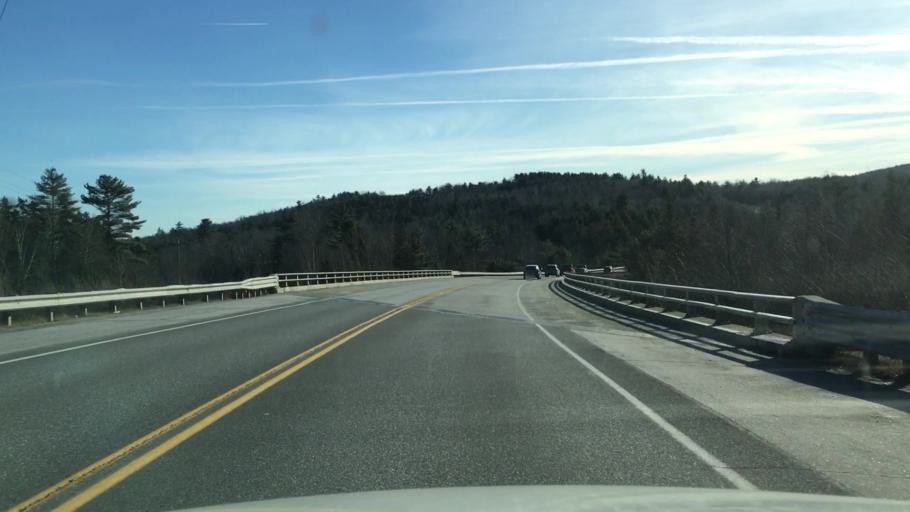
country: US
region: Maine
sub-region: Hancock County
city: Dedham
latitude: 44.6818
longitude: -68.5784
